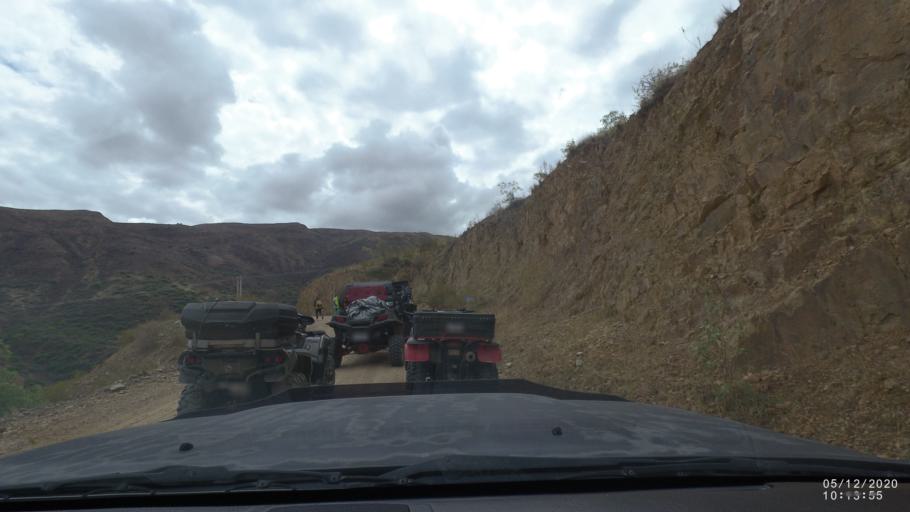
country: BO
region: Cochabamba
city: Sipe Sipe
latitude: -17.4792
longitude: -66.2841
